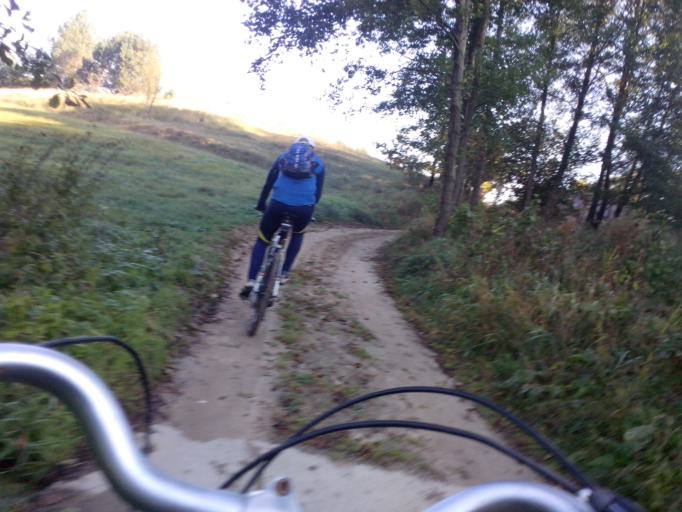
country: PL
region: Kujawsko-Pomorskie
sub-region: Powiat brodnicki
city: Gorzno
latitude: 53.2142
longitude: 19.6560
